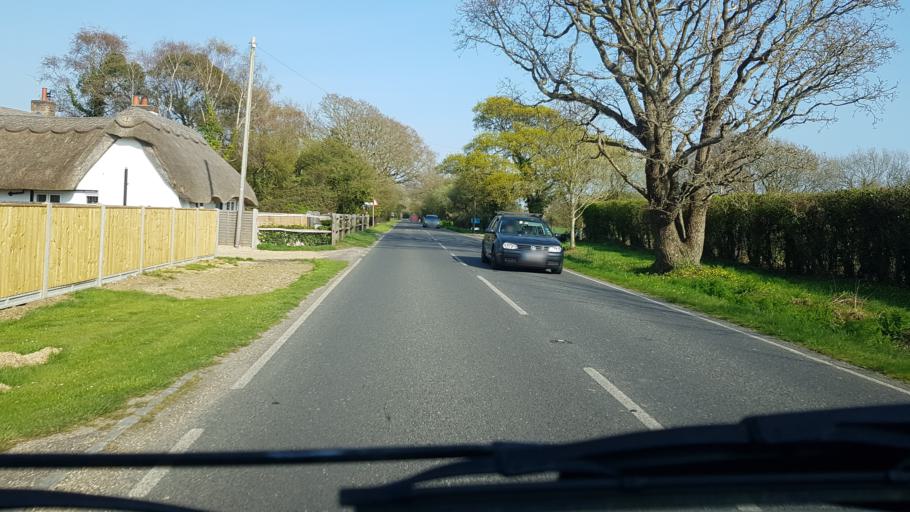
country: GB
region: England
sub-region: West Sussex
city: East Wittering
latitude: 50.7871
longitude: -0.8551
